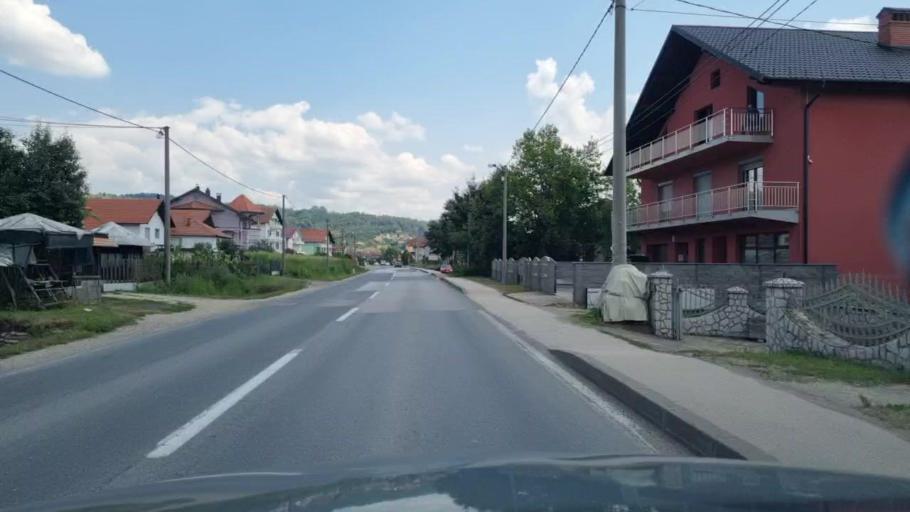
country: BA
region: Federation of Bosnia and Herzegovina
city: Orahovica Donja
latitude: 44.6448
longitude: 18.3685
